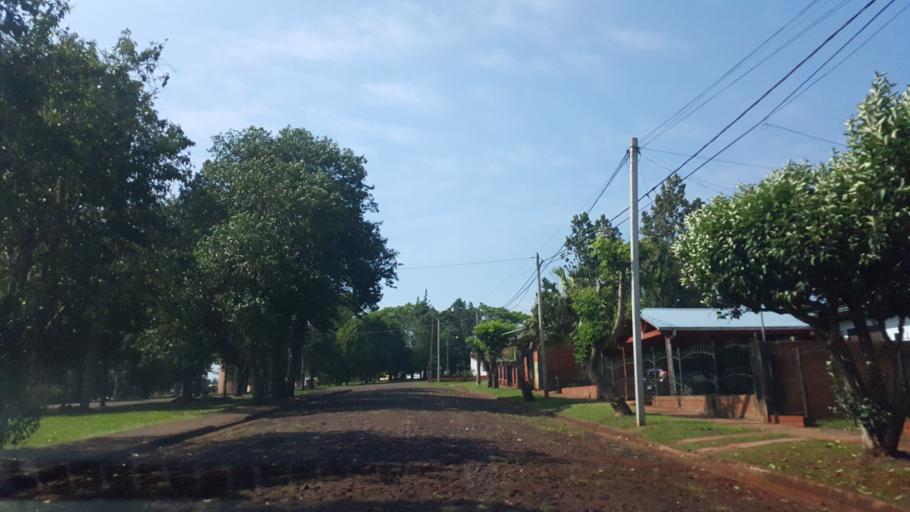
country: AR
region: Misiones
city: Capiovi
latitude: -26.9311
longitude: -55.0558
